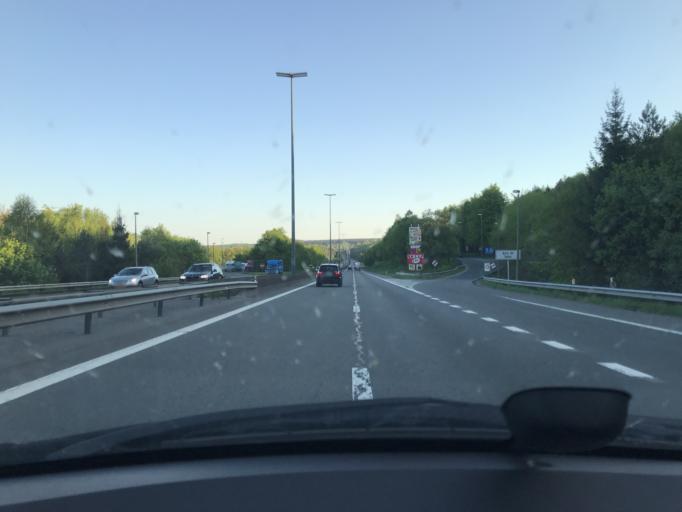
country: BE
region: Wallonia
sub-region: Province du Luxembourg
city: Tellin
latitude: 50.0382
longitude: 5.2116
